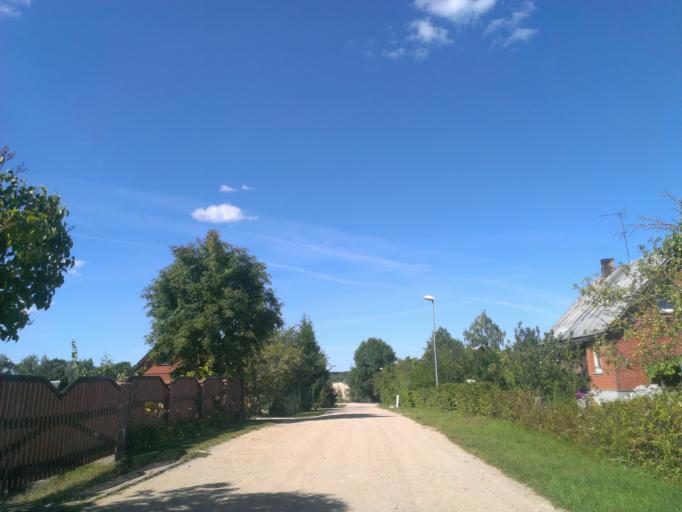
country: LV
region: Malpils
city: Malpils
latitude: 57.0112
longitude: 24.9683
